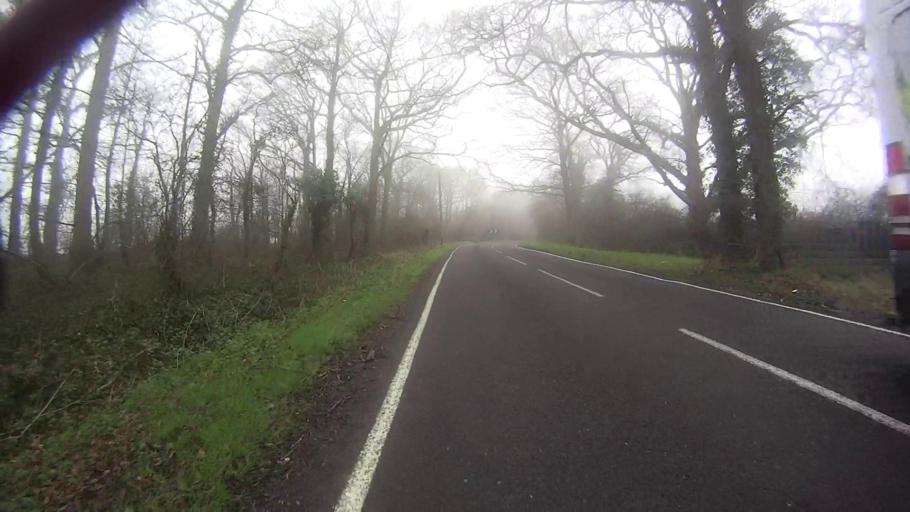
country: GB
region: England
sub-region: Surrey
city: Newdigate
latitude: 51.1359
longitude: -0.3164
